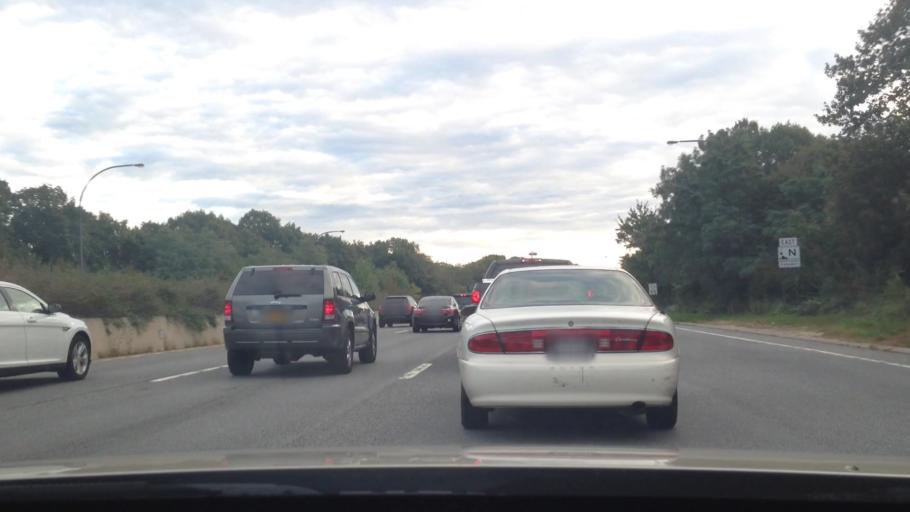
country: US
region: New York
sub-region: Nassau County
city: Westbury
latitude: 40.7655
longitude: -73.5810
